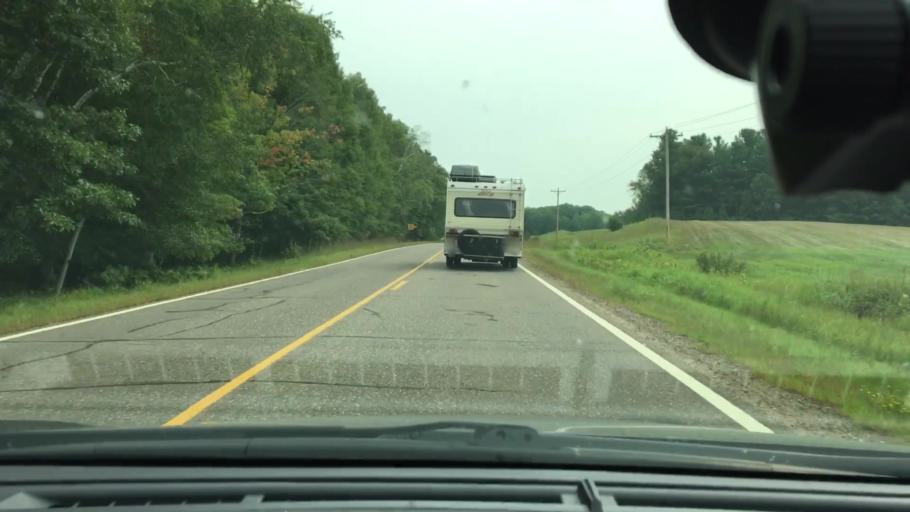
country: US
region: Minnesota
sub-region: Aitkin County
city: Aitkin
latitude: 46.4048
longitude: -93.7875
